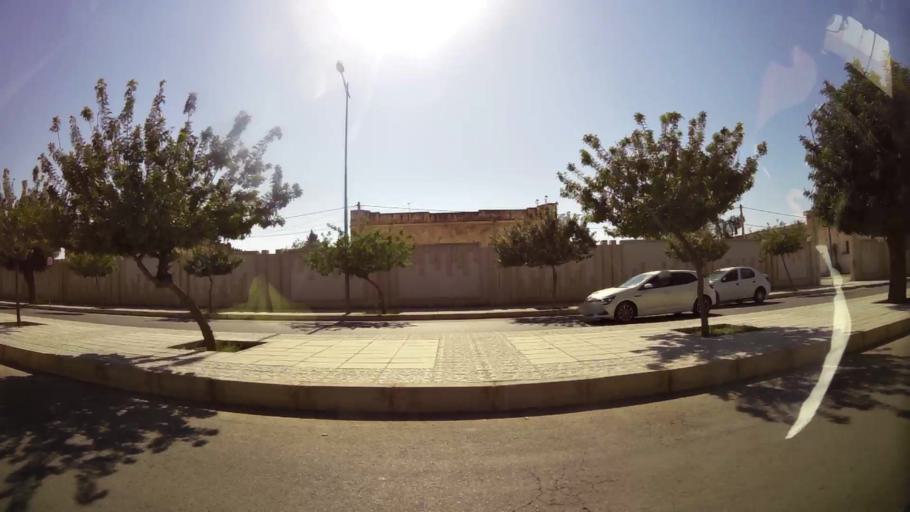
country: MA
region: Oriental
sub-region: Oujda-Angad
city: Oujda
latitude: 34.6913
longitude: -1.9212
